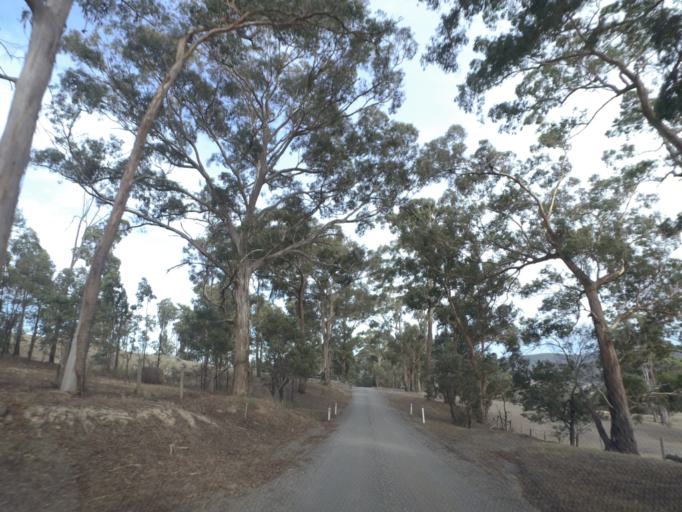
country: AU
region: Victoria
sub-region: Yarra Ranges
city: Yarra Glen
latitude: -37.5955
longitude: 145.3884
